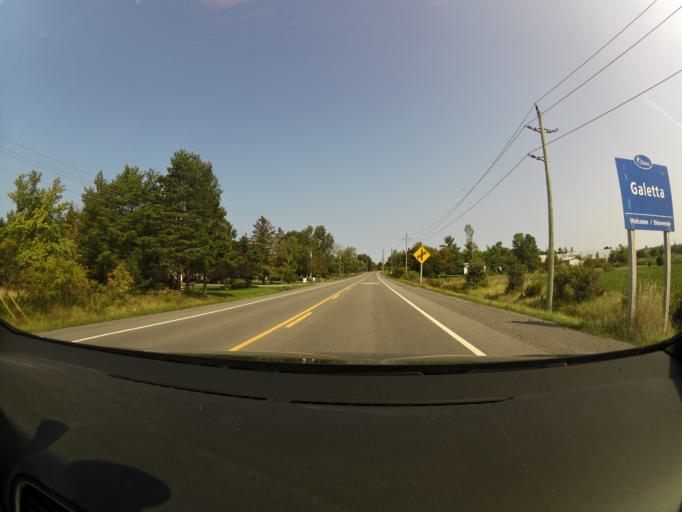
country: CA
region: Ontario
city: Arnprior
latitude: 45.4218
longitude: -76.2603
